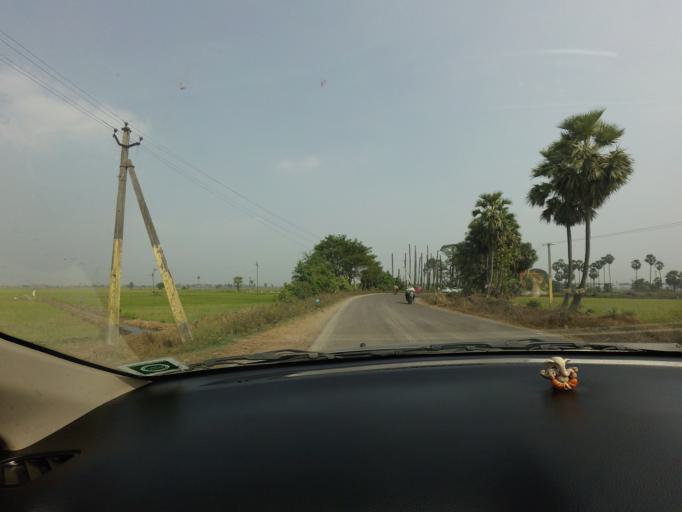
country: IN
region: Andhra Pradesh
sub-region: Krishna
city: Kankipadu
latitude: 16.4546
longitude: 80.7785
